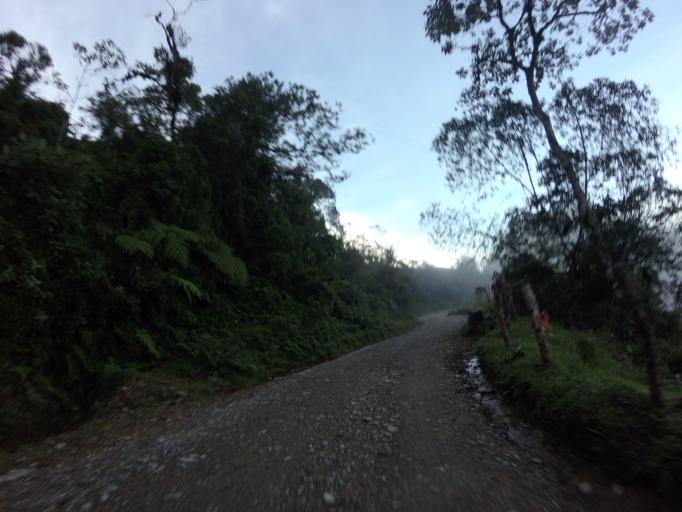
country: CO
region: Caldas
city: Pensilvania
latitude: 5.4333
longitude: -75.1315
